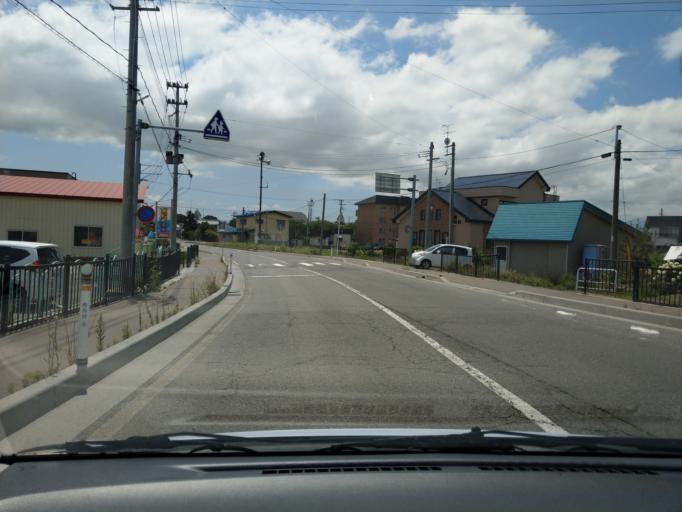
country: JP
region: Aomori
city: Namioka
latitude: 40.6900
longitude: 140.5583
